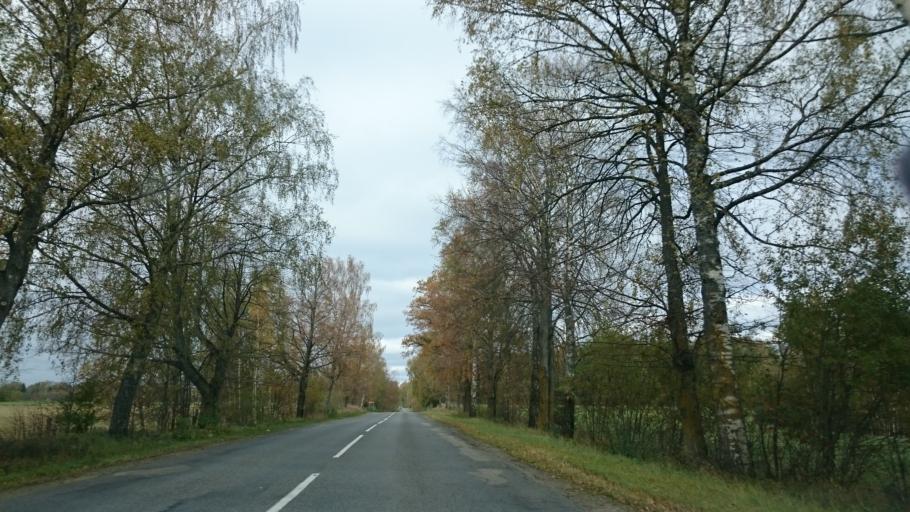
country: LV
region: Amatas Novads
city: Drabesi
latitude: 57.2715
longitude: 25.2727
